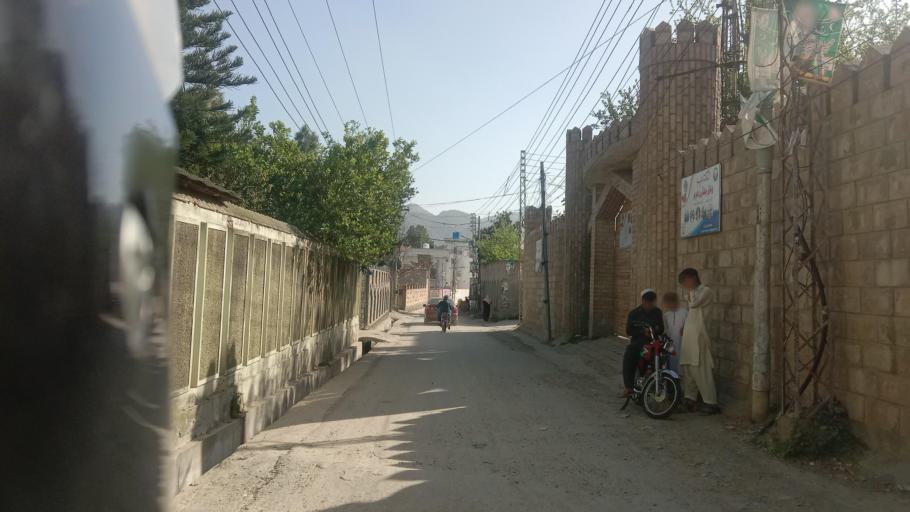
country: PK
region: Khyber Pakhtunkhwa
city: Abbottabad
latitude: 34.1734
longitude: 73.2240
